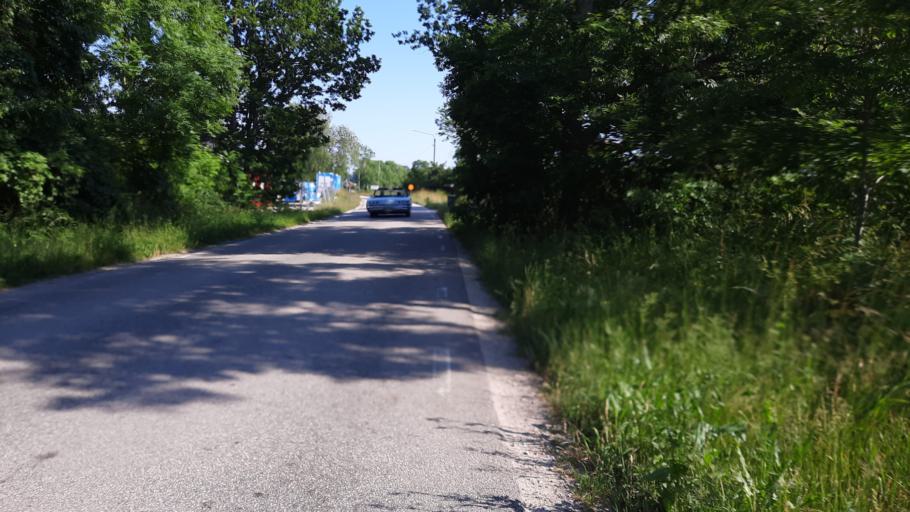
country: SE
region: Blekinge
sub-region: Karlskrona Kommun
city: Sturko
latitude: 56.1112
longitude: 15.6814
